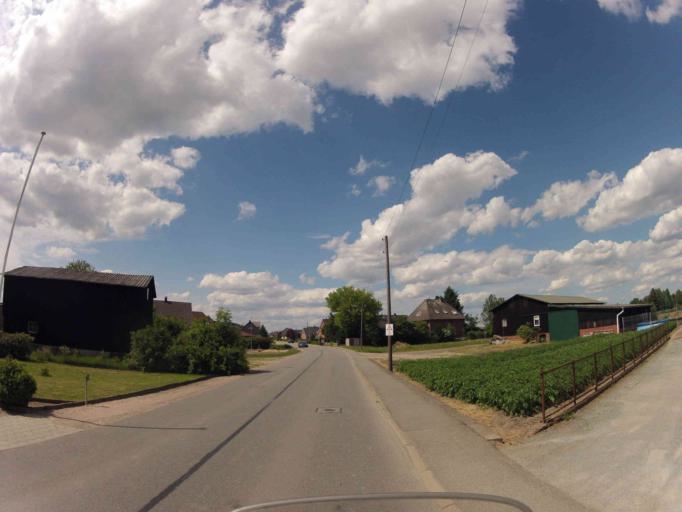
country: DE
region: Hamburg
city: Bergedorf
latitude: 53.4316
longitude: 10.1944
